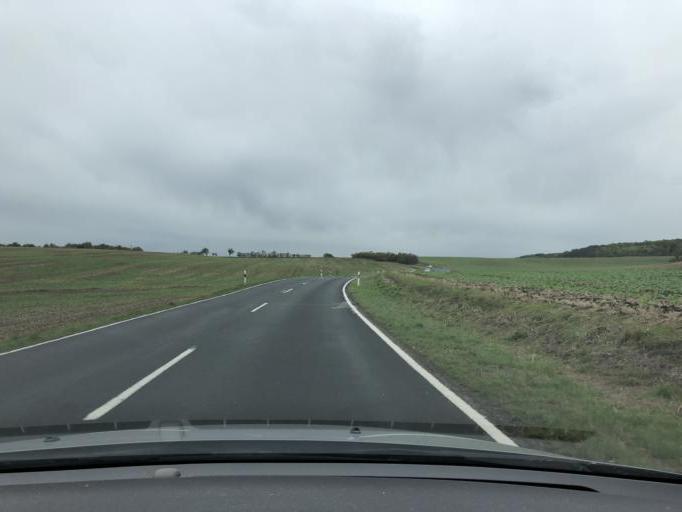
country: DE
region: Saxony-Anhalt
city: Eckartsberga
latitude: 51.1380
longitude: 11.5081
